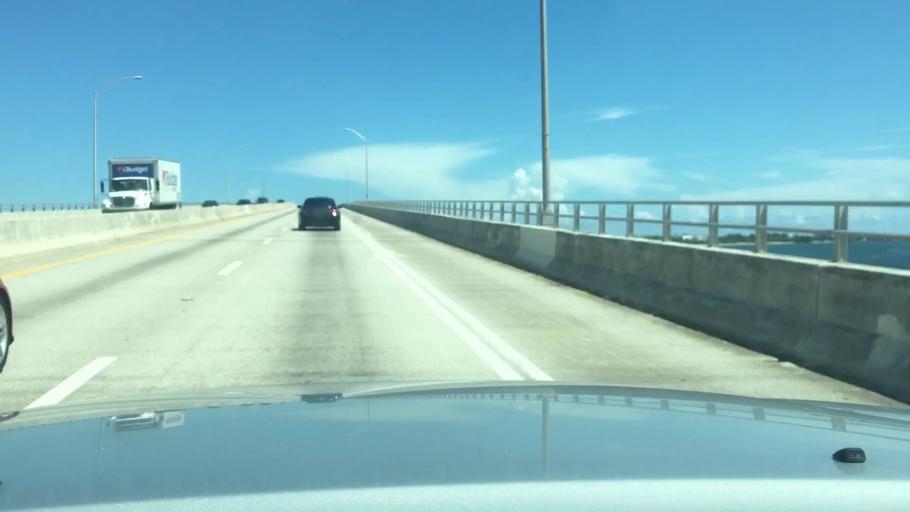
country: US
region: Florida
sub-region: Miami-Dade County
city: Miami
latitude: 25.7463
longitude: -80.1878
